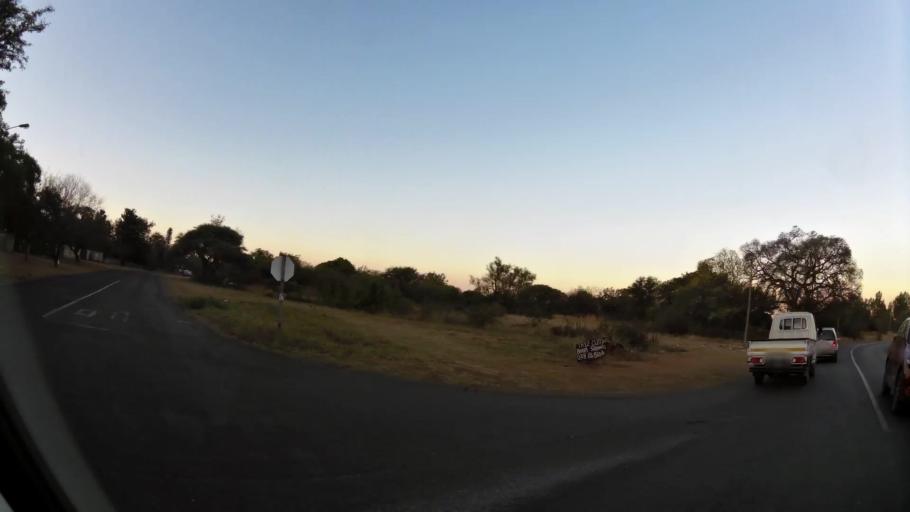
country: ZA
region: North-West
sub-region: Bojanala Platinum District Municipality
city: Rustenburg
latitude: -25.6662
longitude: 27.2148
